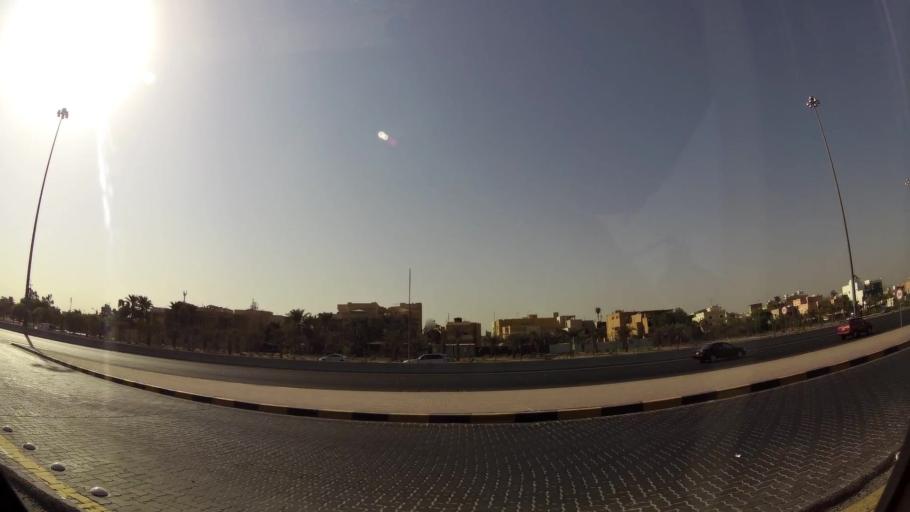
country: KW
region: Al Asimah
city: Ash Shamiyah
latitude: 29.3593
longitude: 47.9672
